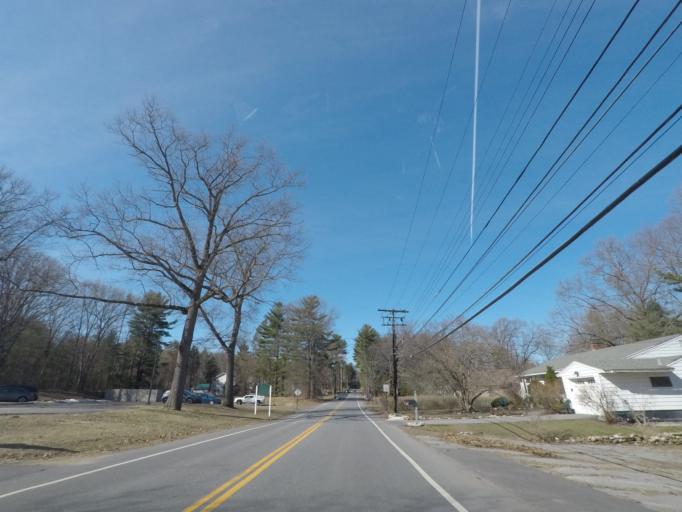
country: US
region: New York
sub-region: Saratoga County
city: North Ballston Spa
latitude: 43.0149
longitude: -73.8486
